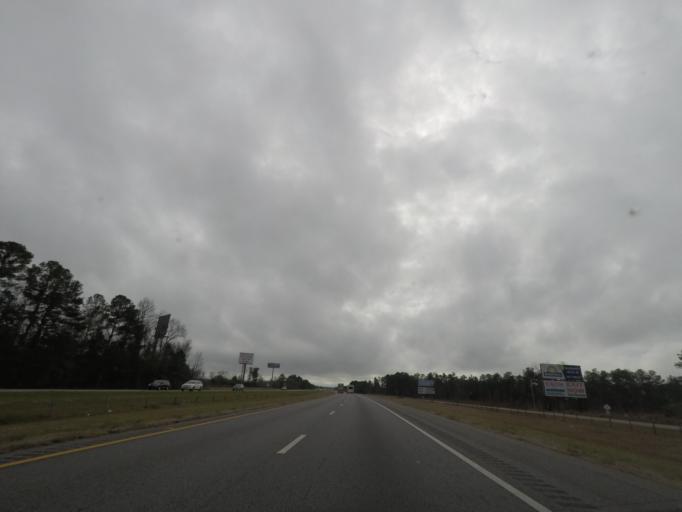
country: US
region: South Carolina
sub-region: Orangeburg County
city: Holly Hill
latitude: 33.3970
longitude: -80.5133
